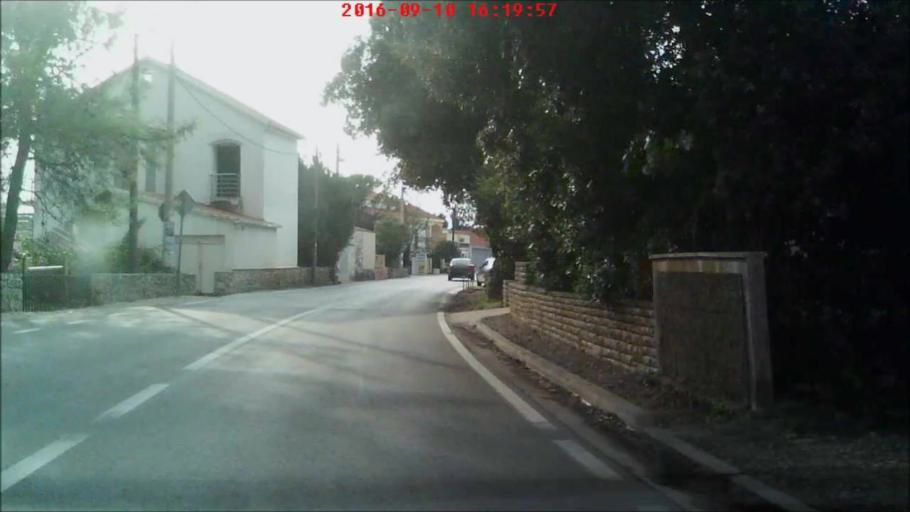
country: HR
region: Zadarska
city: Vir
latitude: 44.2996
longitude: 15.0896
